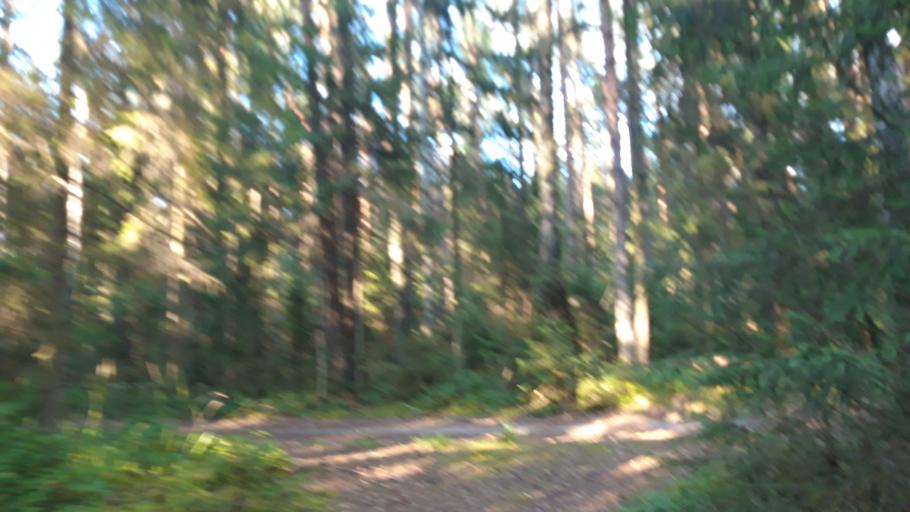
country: RU
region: Tverskaya
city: Konakovo
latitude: 56.6762
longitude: 36.6921
